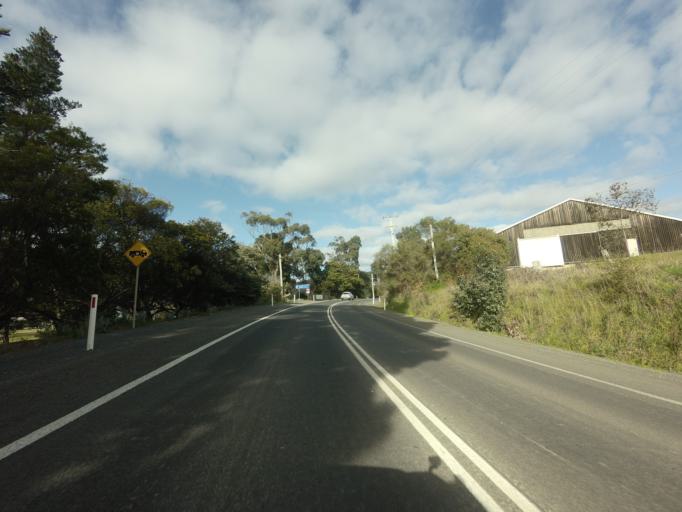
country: AU
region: Tasmania
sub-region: Huon Valley
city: Geeveston
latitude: -43.1578
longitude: 146.9795
